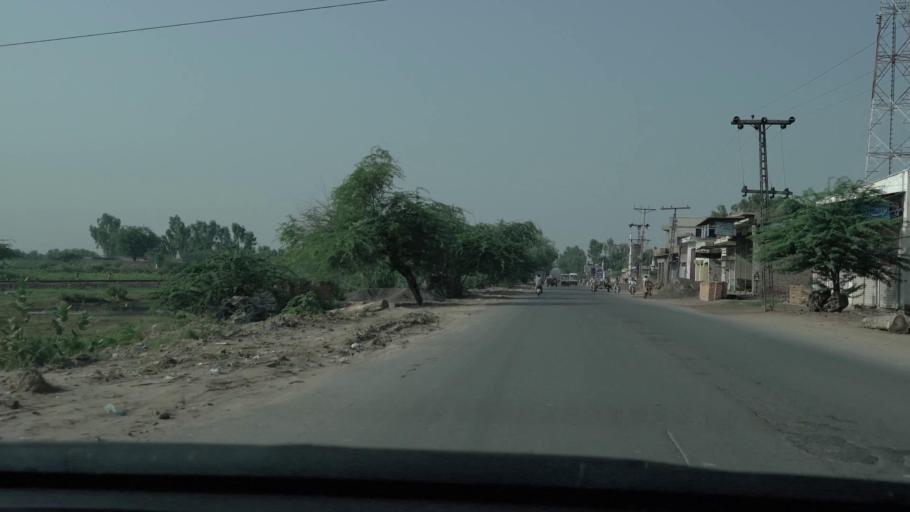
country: PK
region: Punjab
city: Gojra
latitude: 31.1220
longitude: 72.6701
